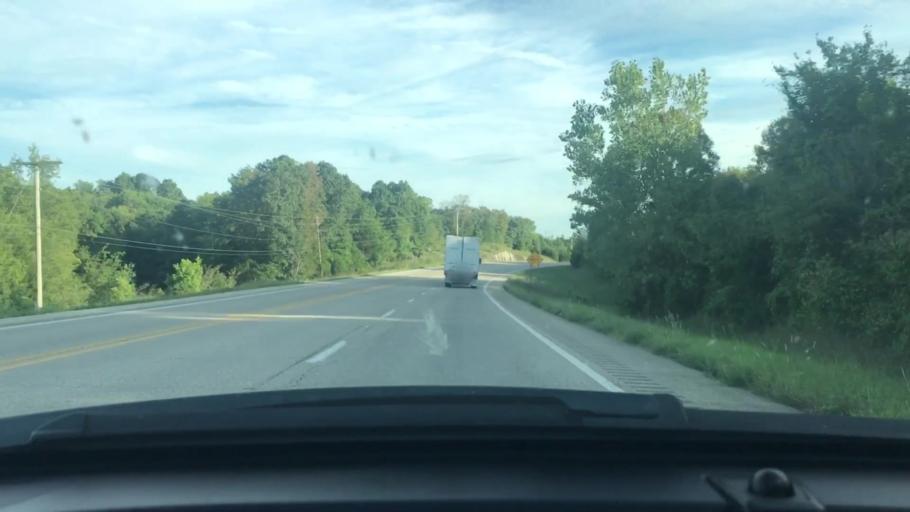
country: US
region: Arkansas
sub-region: Randolph County
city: Pocahontas
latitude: 36.1888
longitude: -91.1635
